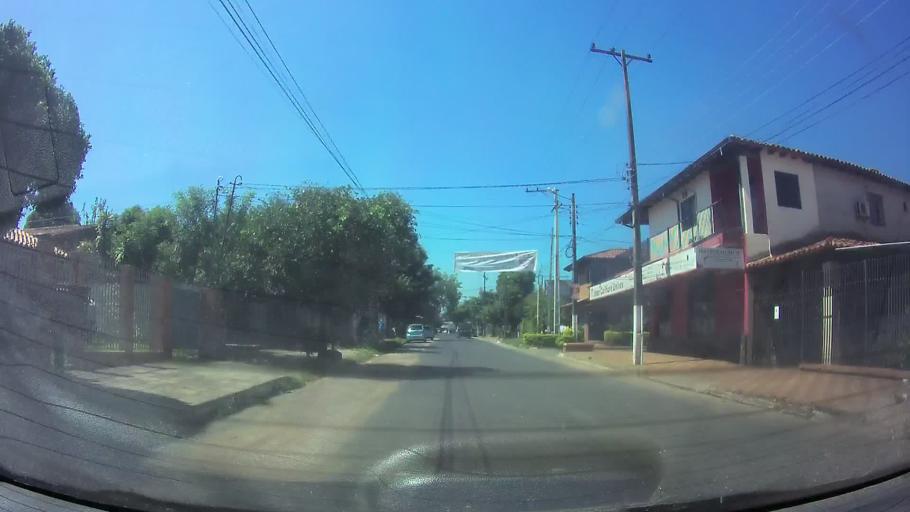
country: PY
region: Central
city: Fernando de la Mora
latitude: -25.3001
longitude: -57.5283
